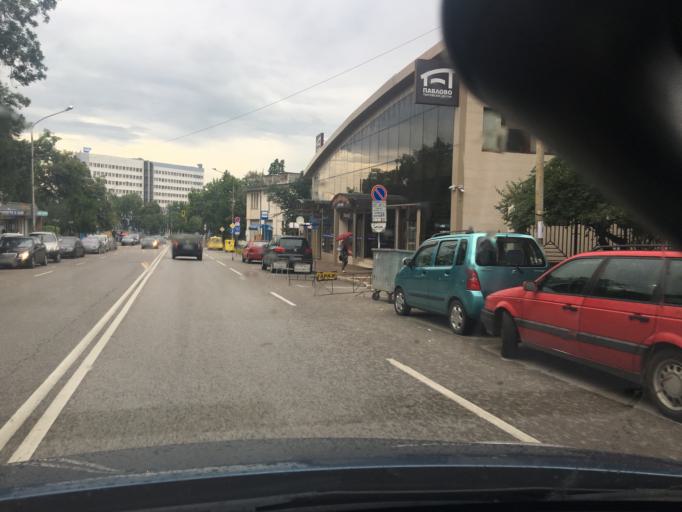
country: BG
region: Sofia-Capital
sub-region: Stolichna Obshtina
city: Sofia
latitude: 42.6664
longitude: 23.2661
